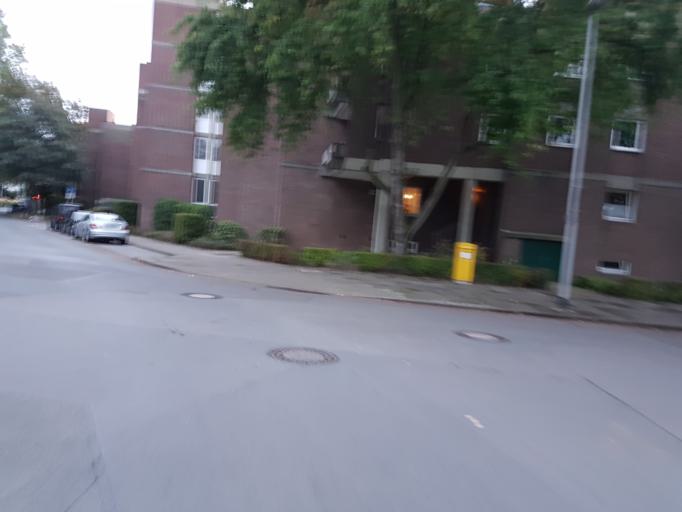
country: DE
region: Lower Saxony
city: Hannover
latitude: 52.3966
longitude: 9.7526
